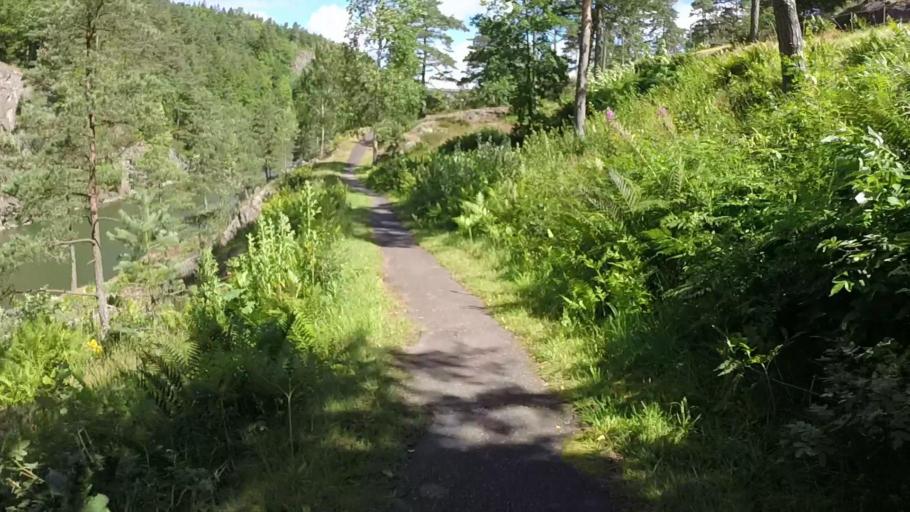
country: SE
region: Vaestra Goetaland
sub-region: Trollhattan
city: Trollhattan
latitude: 58.2767
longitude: 12.2740
